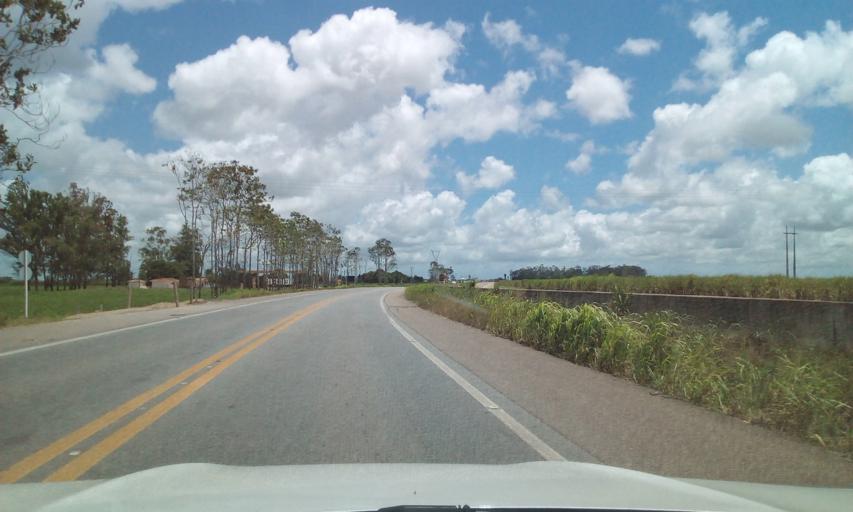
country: BR
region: Alagoas
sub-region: Campo Alegre
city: Campo Alegre
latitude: -9.9000
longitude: -36.2512
